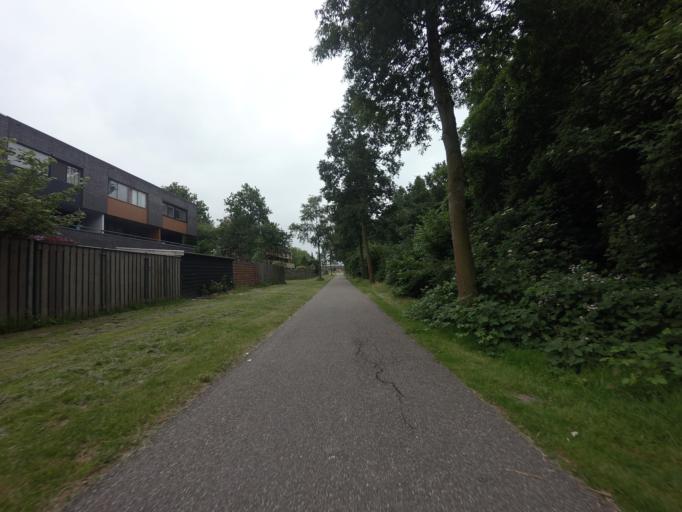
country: NL
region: Flevoland
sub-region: Gemeente Almere
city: Almere Stad
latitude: 52.3995
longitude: 5.2834
